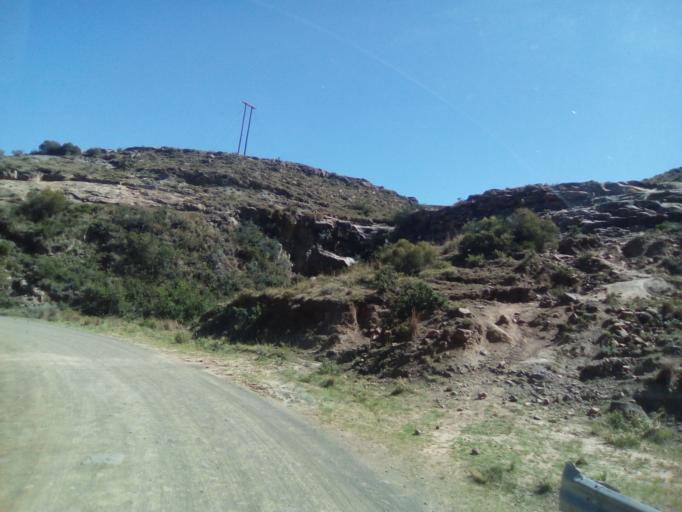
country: LS
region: Qacha's Nek
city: Qacha's Nek
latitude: -30.0418
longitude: 28.6615
